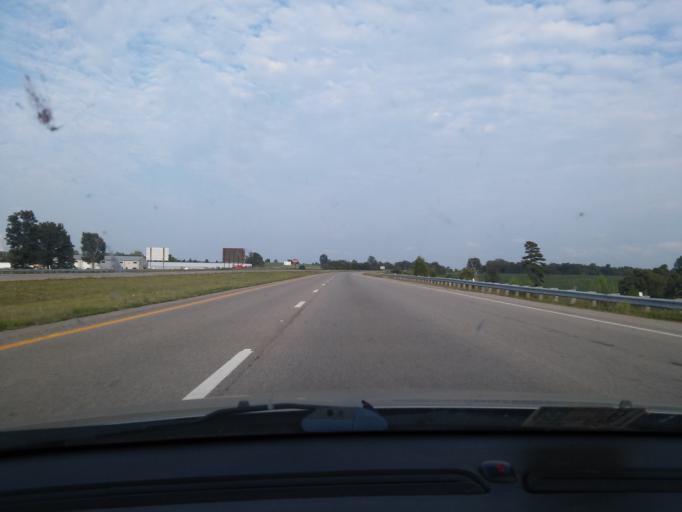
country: US
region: Ohio
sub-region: Gallia County
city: Gallipolis
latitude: 38.8761
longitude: -82.2936
